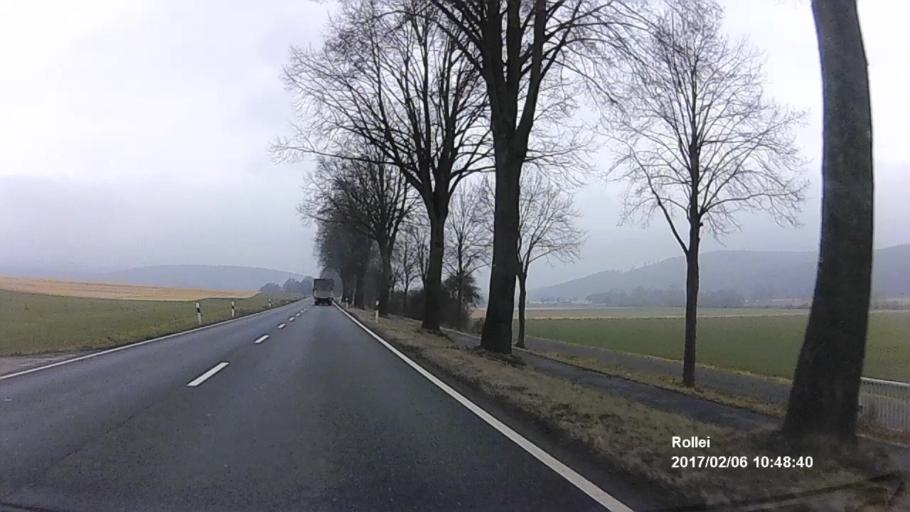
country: DE
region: Lower Saxony
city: Katlenburg-Lindau
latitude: 51.6931
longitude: 10.0740
